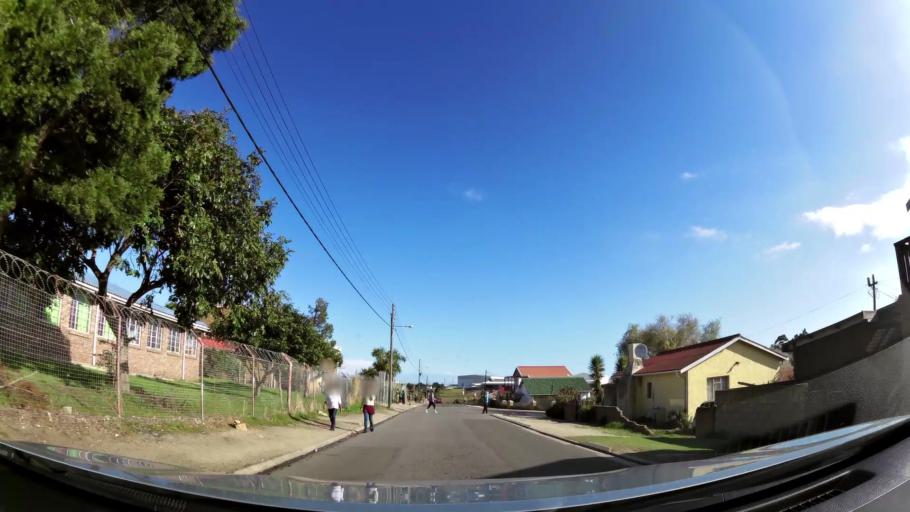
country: ZA
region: Western Cape
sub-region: Eden District Municipality
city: George
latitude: -33.9743
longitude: 22.4774
